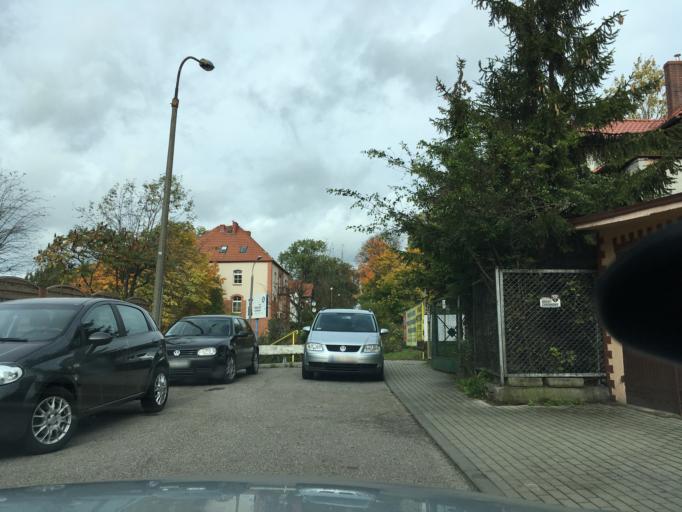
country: PL
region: Pomeranian Voivodeship
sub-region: Powiat koscierski
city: Koscierzyna
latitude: 54.1219
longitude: 17.9819
